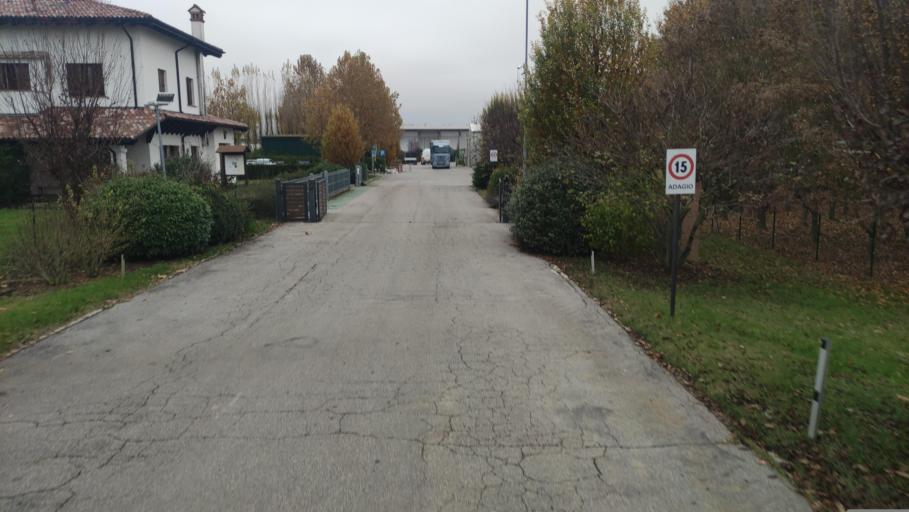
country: IT
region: Emilia-Romagna
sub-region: Provincia di Bologna
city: Baricella
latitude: 44.6292
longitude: 11.5351
